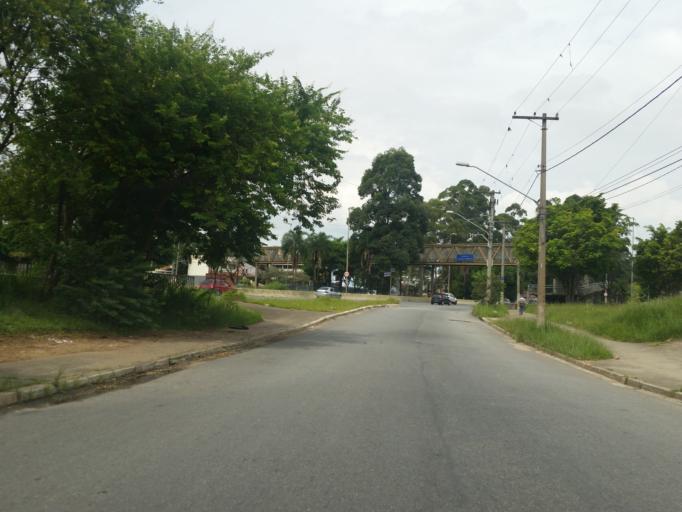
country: BR
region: Sao Paulo
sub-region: Ferraz De Vasconcelos
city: Ferraz de Vasconcelos
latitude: -23.5373
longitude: -46.4519
